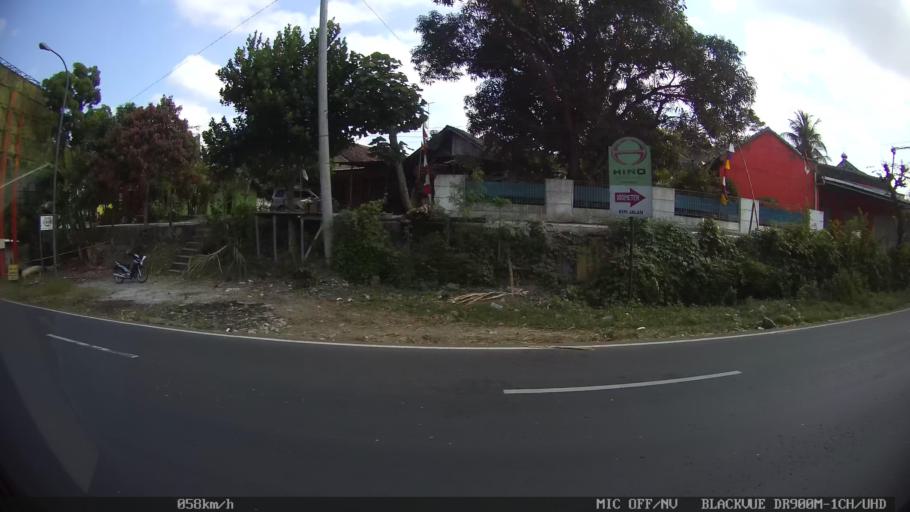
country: ID
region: Daerah Istimewa Yogyakarta
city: Godean
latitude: -7.8219
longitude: 110.2366
